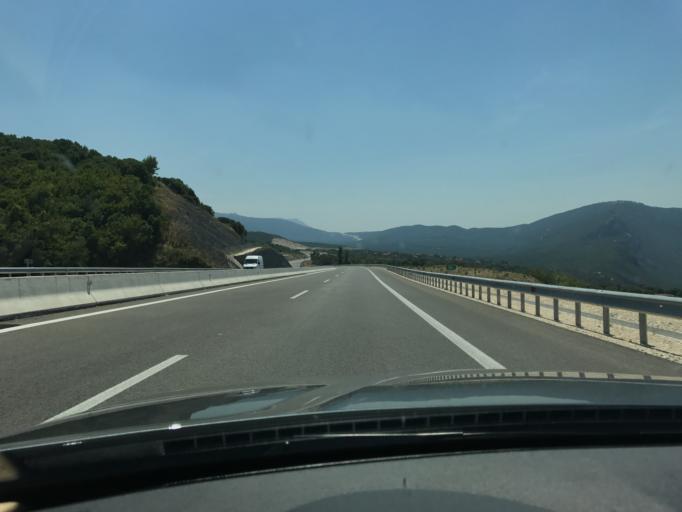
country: GR
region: Epirus
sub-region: Nomos Ioanninon
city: Agia Kyriaki
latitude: 39.4840
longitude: 20.8927
